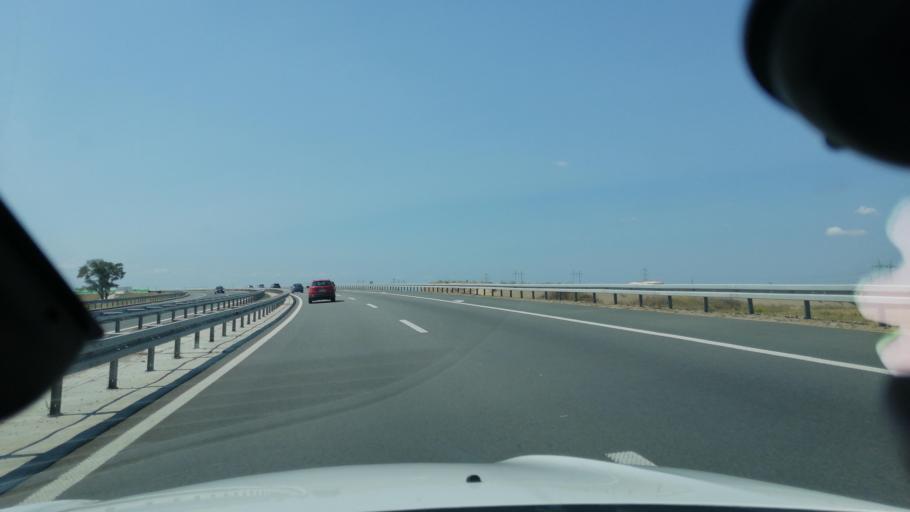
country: RS
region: Central Serbia
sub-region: Belgrade
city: Surcin
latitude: 44.7686
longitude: 20.2507
